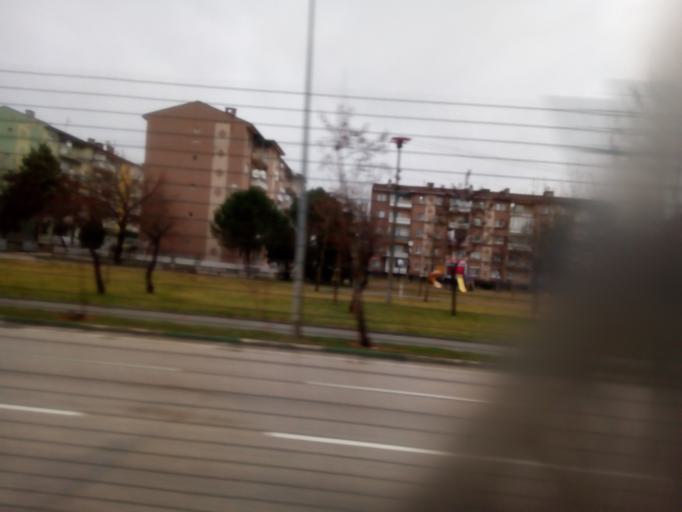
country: TR
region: Bursa
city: Niluefer
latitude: 40.2463
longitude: 28.9633
